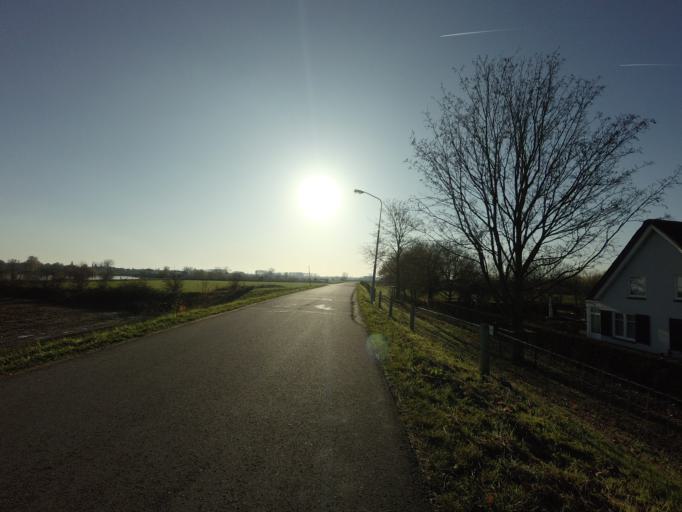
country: NL
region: North Brabant
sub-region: Gemeente 's-Hertogenbosch
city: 's-Hertogenbosch
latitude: 51.7589
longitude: 5.3416
